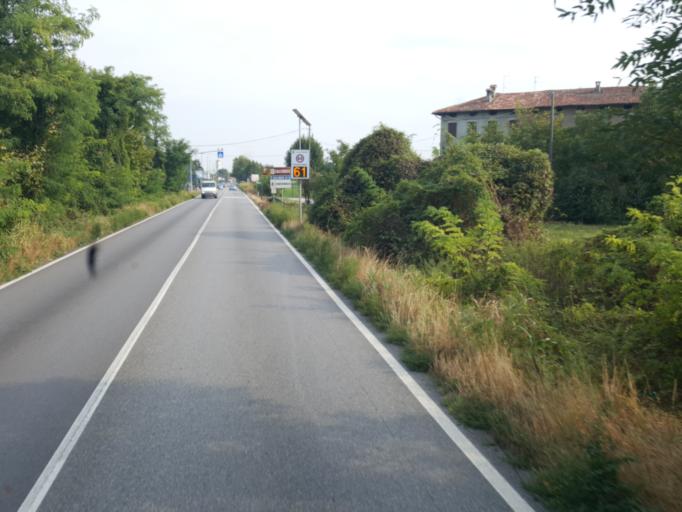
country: IT
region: Lombardy
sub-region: Provincia di Bergamo
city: Cavernago
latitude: 45.6364
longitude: 9.7584
